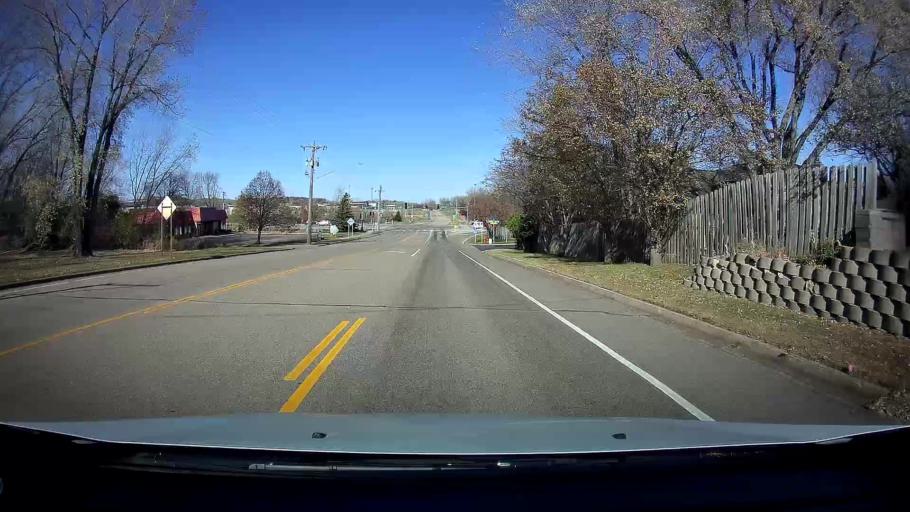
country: US
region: Minnesota
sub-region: Ramsey County
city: Shoreview
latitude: 45.0778
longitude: -93.1575
